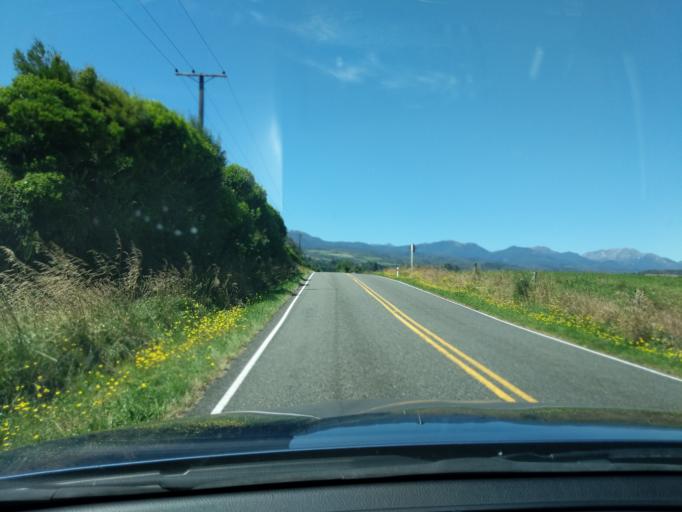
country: NZ
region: Tasman
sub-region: Tasman District
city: Takaka
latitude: -40.7093
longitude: 172.6369
